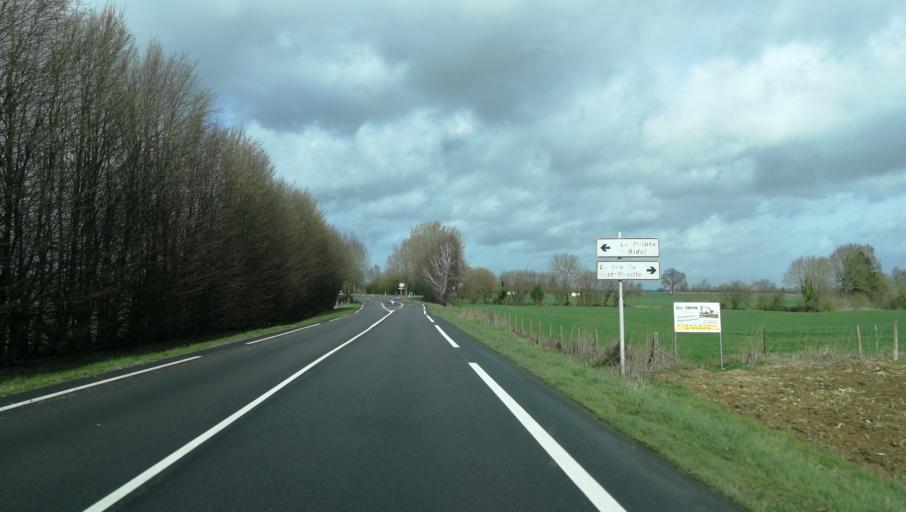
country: FR
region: Haute-Normandie
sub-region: Departement de l'Eure
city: Beuzeville
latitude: 49.3088
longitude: 0.3861
